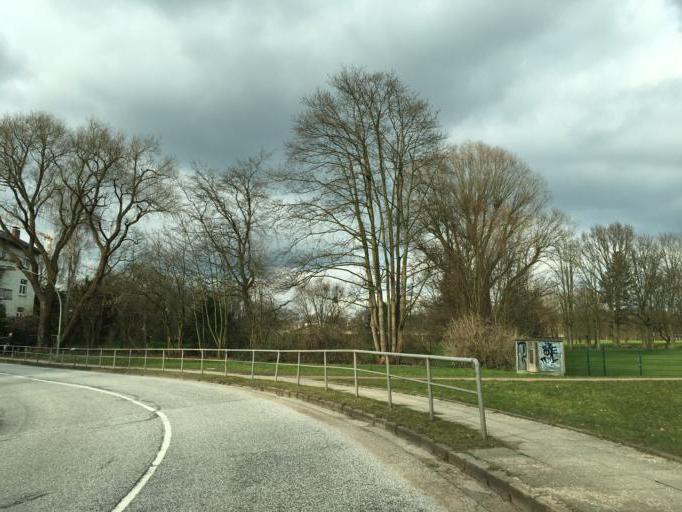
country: DE
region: Hamburg
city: Altona
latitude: 53.5546
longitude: 9.8733
